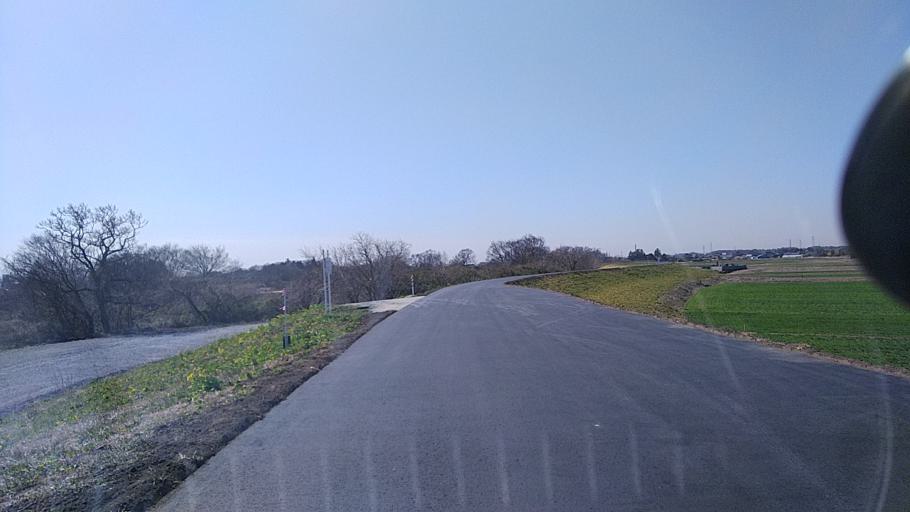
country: JP
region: Ibaraki
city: Ishige
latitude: 36.0955
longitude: 140.0042
